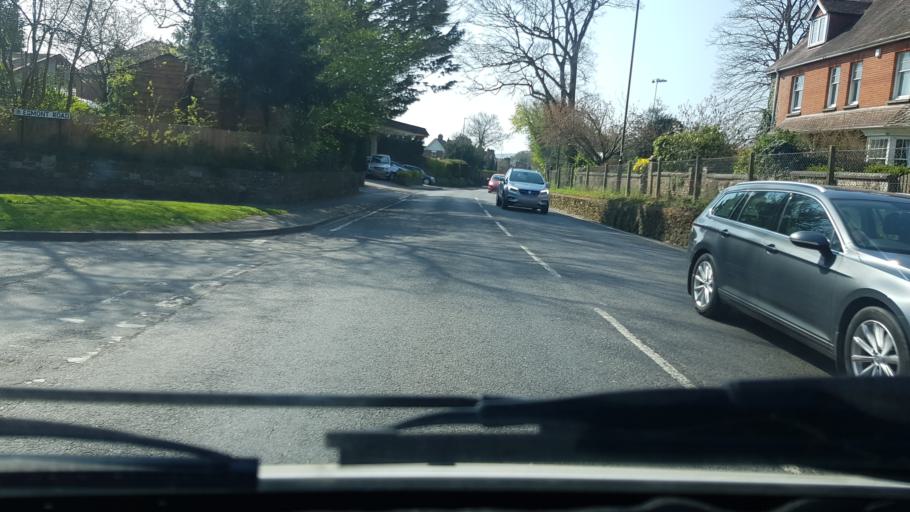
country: GB
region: England
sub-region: West Sussex
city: Midhurst
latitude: 50.9954
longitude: -0.7320
